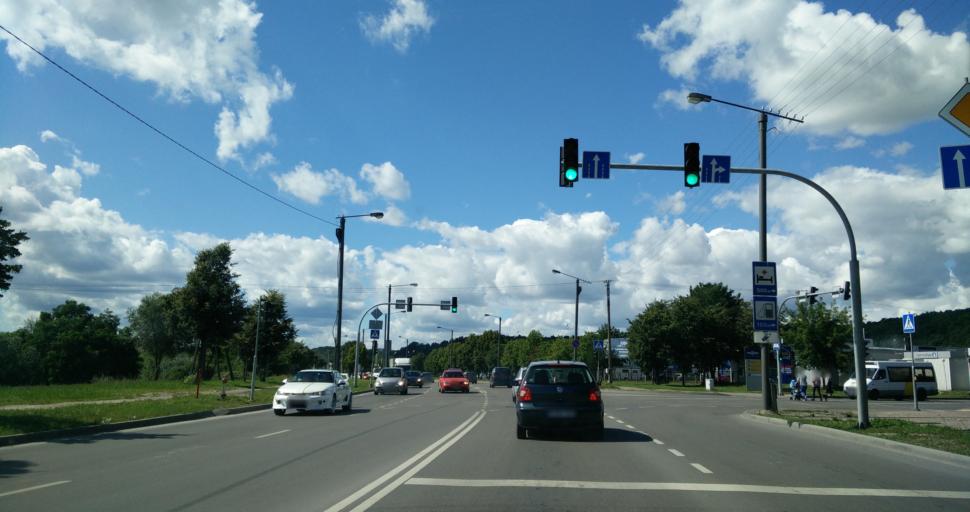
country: LT
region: Kauno apskritis
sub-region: Kauno rajonas
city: Akademija (Kaunas)
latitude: 54.9200
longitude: 23.8275
